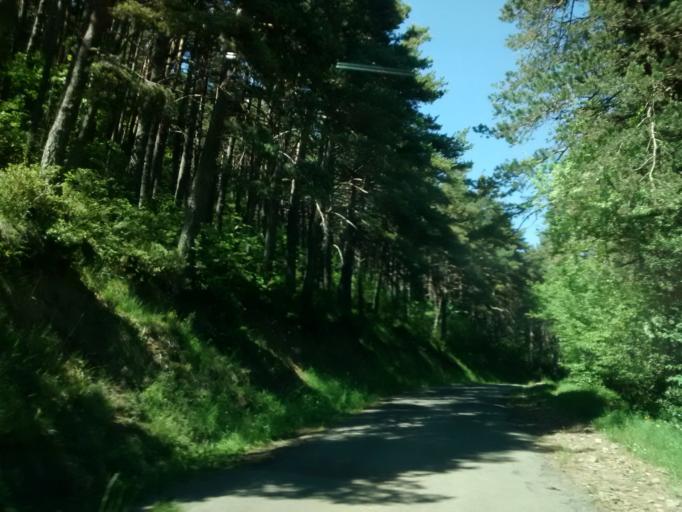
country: ES
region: Aragon
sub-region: Provincia de Huesca
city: Borau
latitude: 42.7093
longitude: -0.6100
